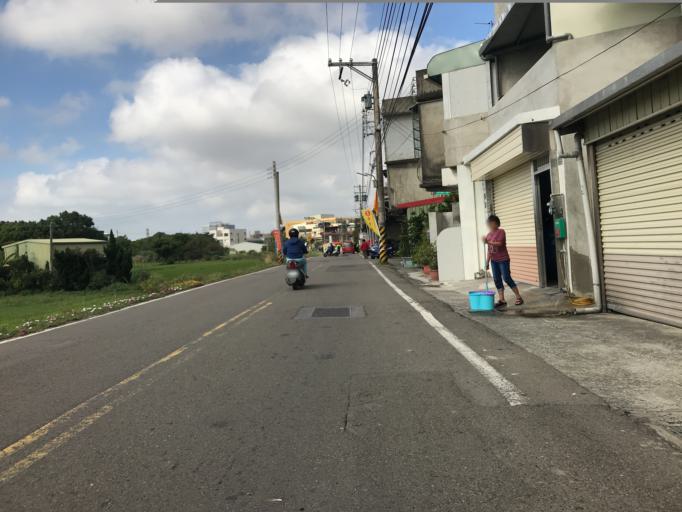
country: TW
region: Taiwan
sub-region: Hsinchu
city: Zhubei
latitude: 24.8077
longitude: 121.0058
